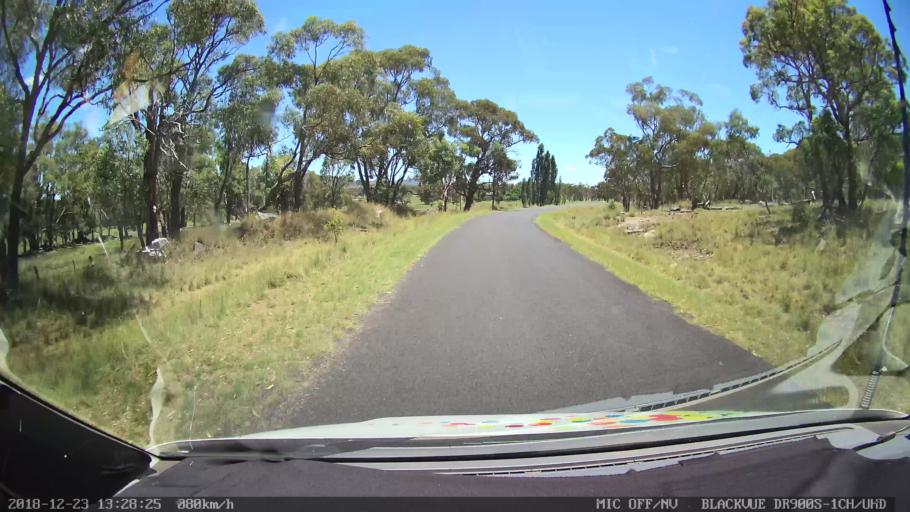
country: AU
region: New South Wales
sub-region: Armidale Dumaresq
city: Armidale
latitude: -30.4668
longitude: 151.3490
